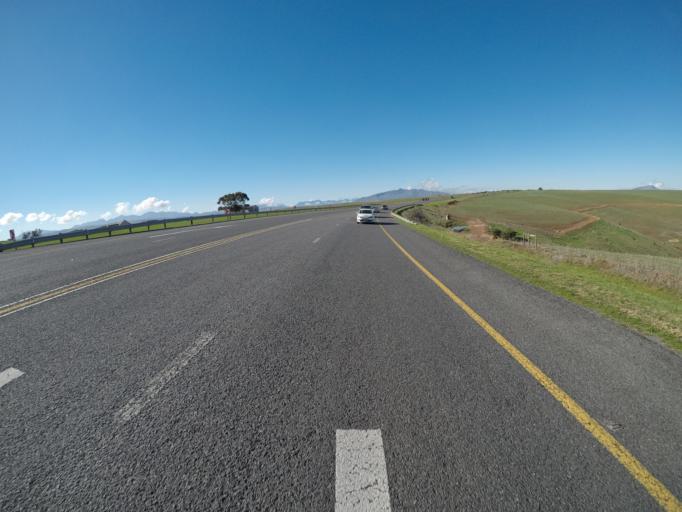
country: ZA
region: Western Cape
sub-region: Overberg District Municipality
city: Caledon
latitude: -34.2228
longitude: 19.2812
